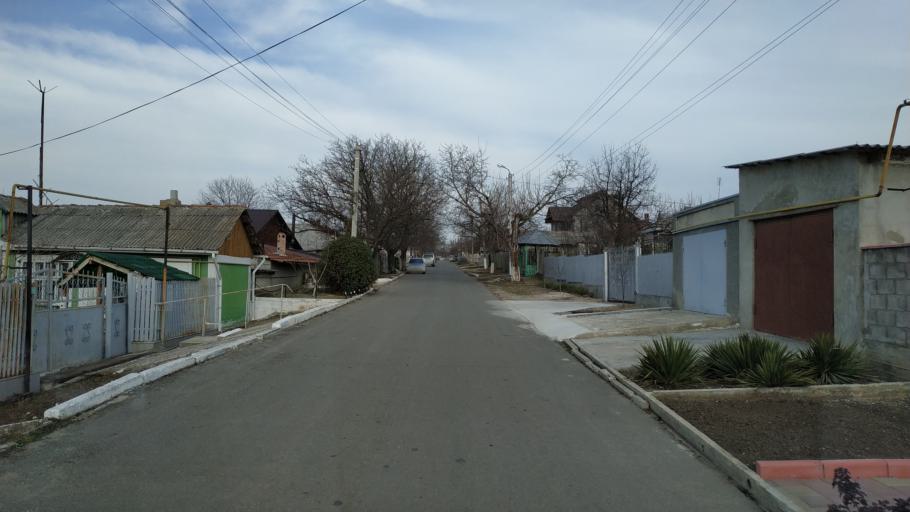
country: MD
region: Chisinau
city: Vatra
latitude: 46.9826
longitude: 28.6745
